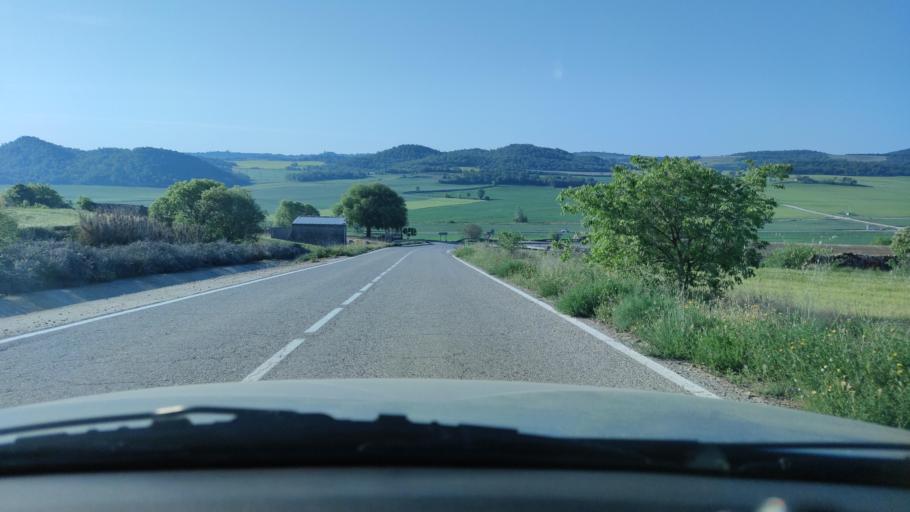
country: ES
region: Catalonia
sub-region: Provincia de Lleida
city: Artesa de Segre
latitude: 41.8747
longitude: 1.0167
